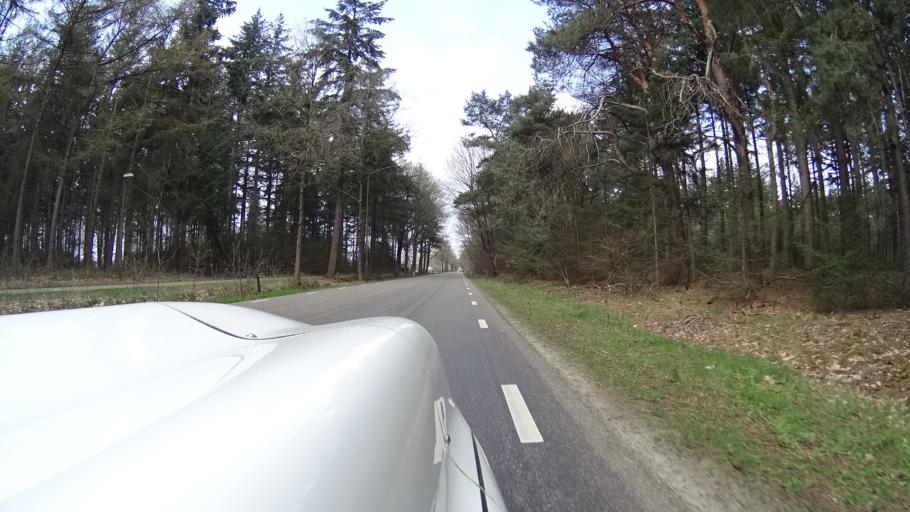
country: NL
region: North Brabant
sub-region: Gemeente Veghel
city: Keldonk
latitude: 51.5455
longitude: 5.5659
